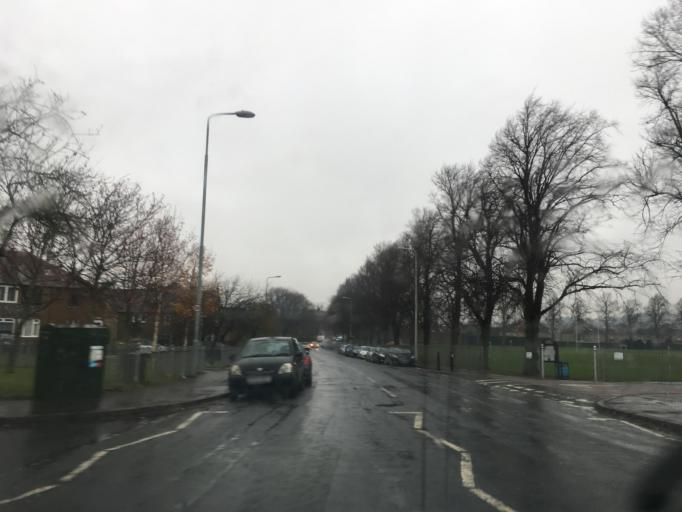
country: GB
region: Scotland
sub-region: Edinburgh
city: Colinton
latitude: 55.9343
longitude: -3.2766
